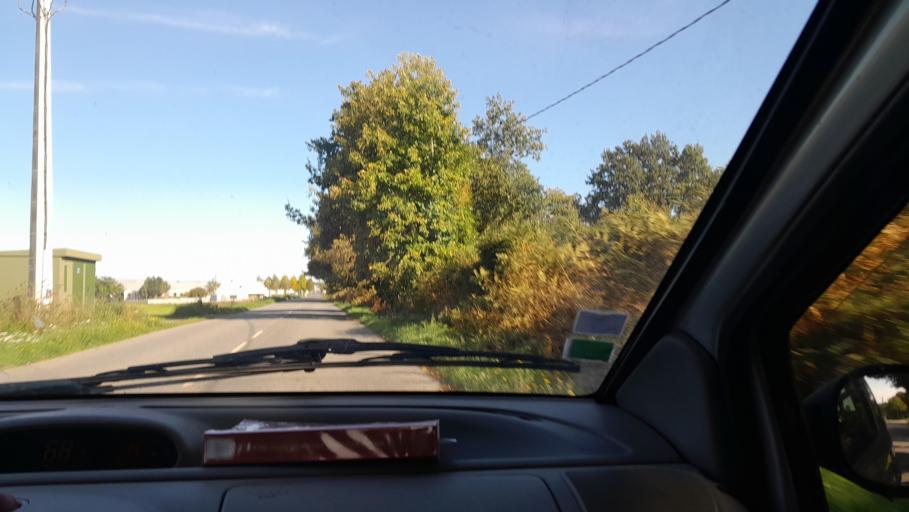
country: FR
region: Brittany
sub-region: Departement d'Ille-et-Vilaine
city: Etrelles
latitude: 48.0564
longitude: -1.1747
